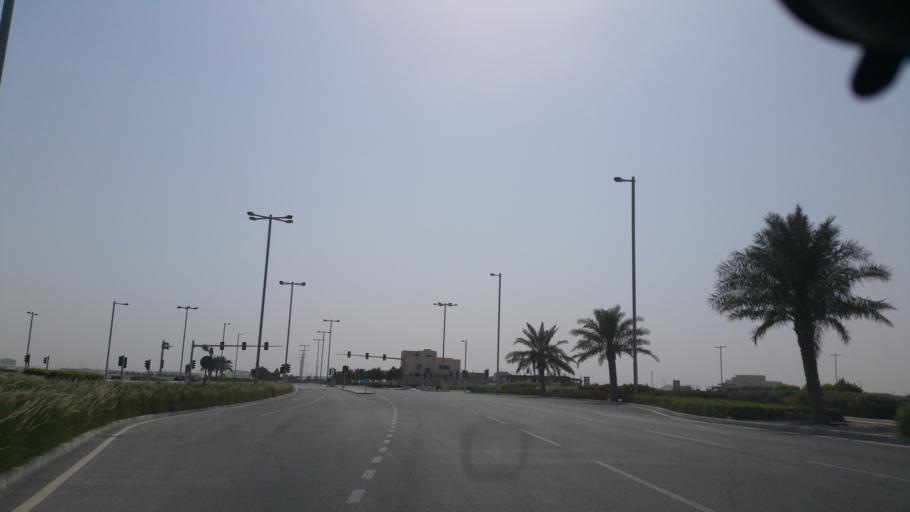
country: QA
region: Baladiyat Umm Salal
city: Umm Salal Muhammad
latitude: 25.4412
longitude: 51.5087
